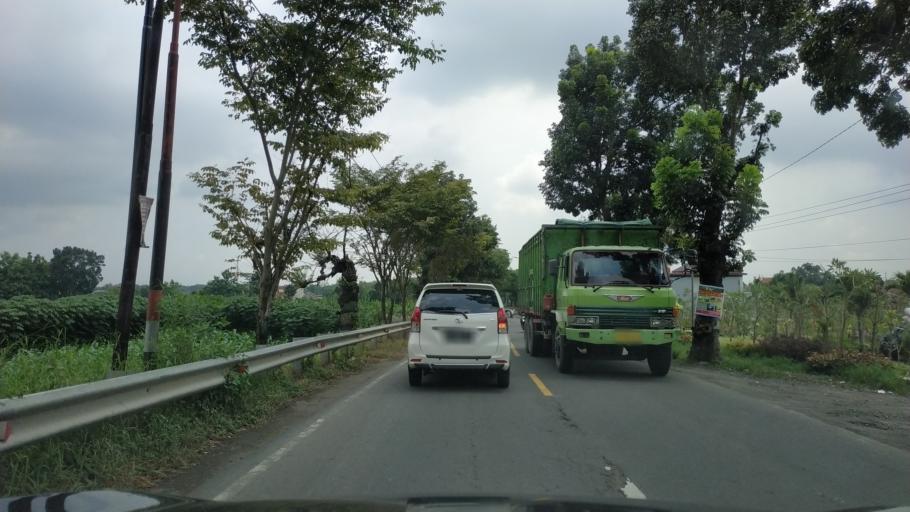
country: ID
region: Central Java
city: Lebaksiu
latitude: -7.0168
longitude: 109.1421
